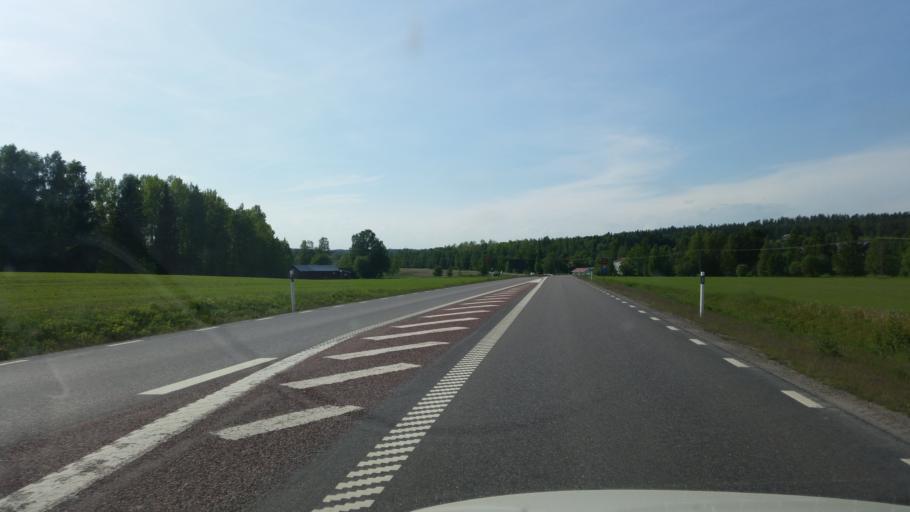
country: SE
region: Gaevleborg
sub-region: Hudiksvalls Kommun
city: Sorforsa
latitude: 61.7301
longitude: 16.9627
